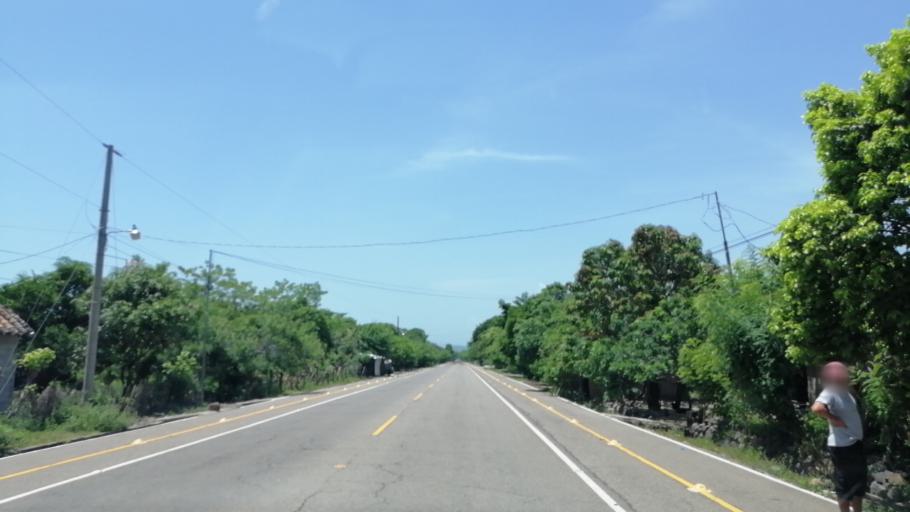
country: SV
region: Chalatenango
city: Nueva Concepcion
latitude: 14.1437
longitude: -89.3005
